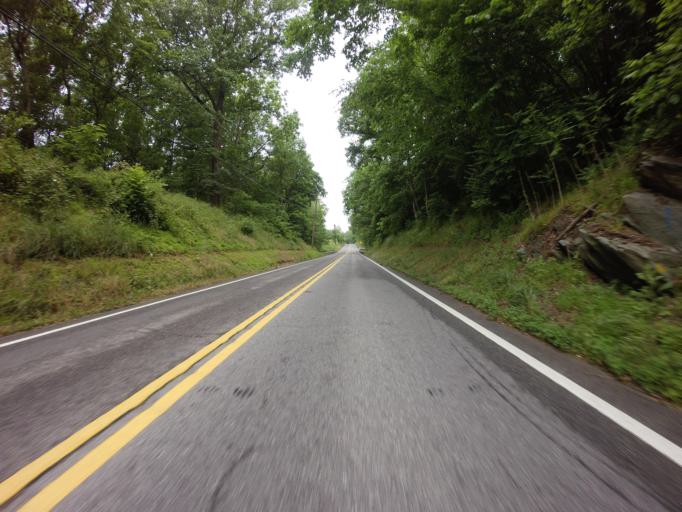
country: US
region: Maryland
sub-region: Frederick County
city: Jefferson
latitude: 39.3329
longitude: -77.5684
